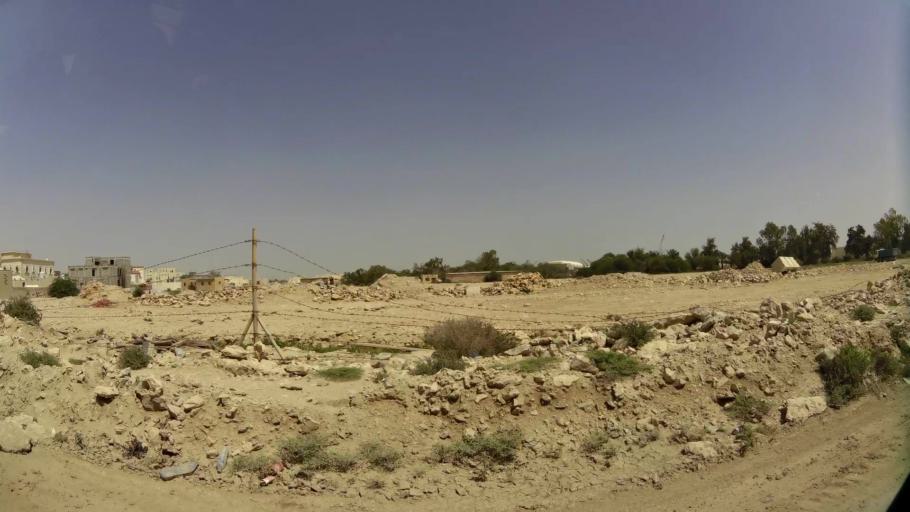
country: QA
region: Baladiyat Umm Salal
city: Umm Salal Muhammad
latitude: 25.3725
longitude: 51.4563
